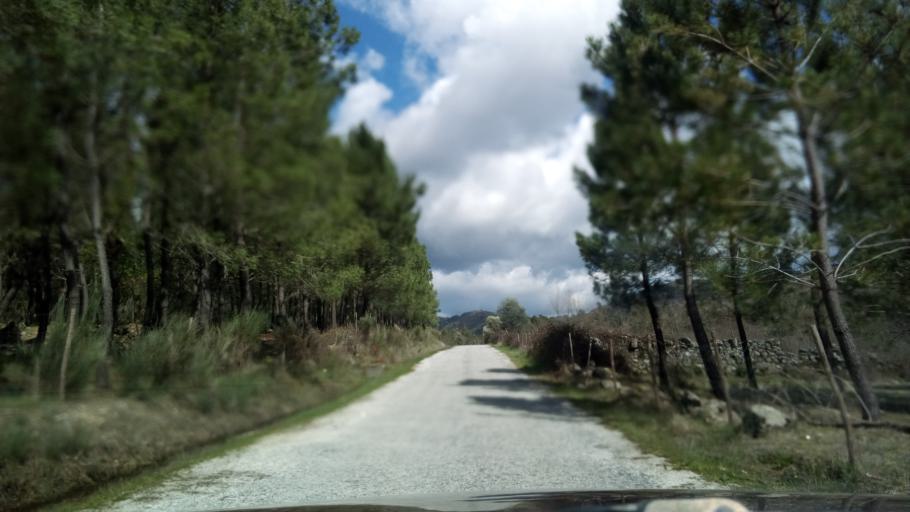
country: PT
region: Guarda
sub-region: Fornos de Algodres
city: Fornos de Algodres
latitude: 40.6501
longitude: -7.5022
